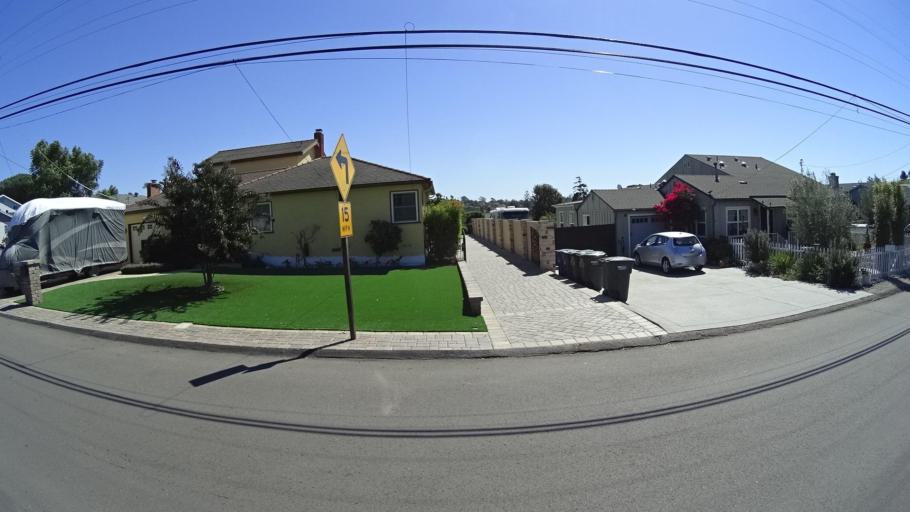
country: US
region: California
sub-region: San Diego County
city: Bonita
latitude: 32.6558
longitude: -117.0553
